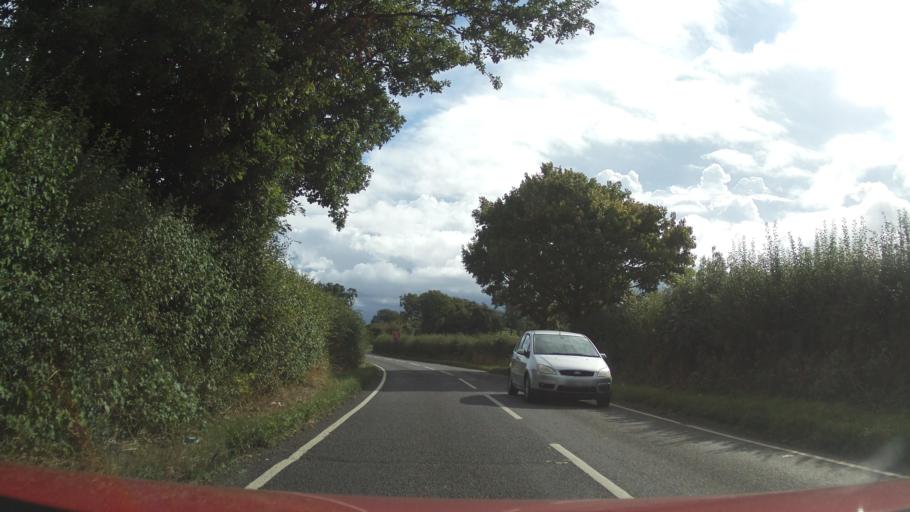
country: GB
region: England
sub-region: Telford and Wrekin
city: Madeley
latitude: 52.6312
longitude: -2.4133
